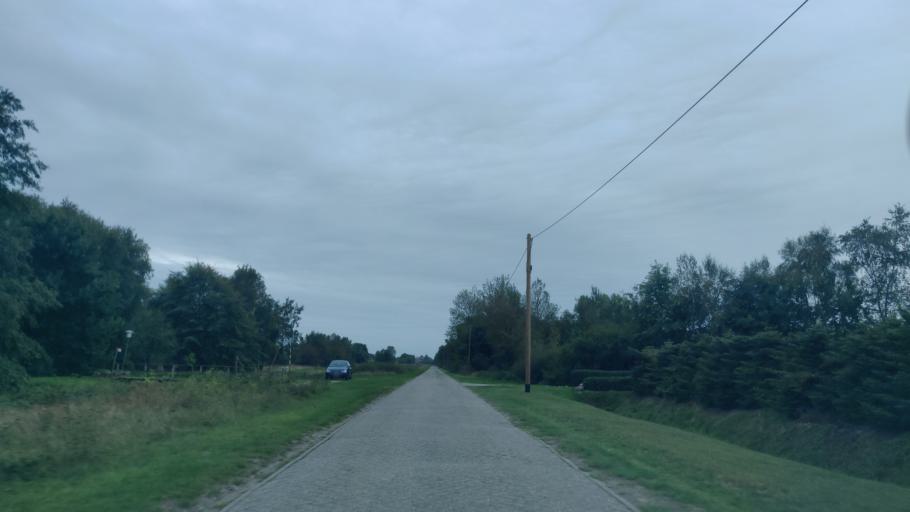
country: DE
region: Lower Saxony
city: Aurich
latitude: 53.4902
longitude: 7.4143
